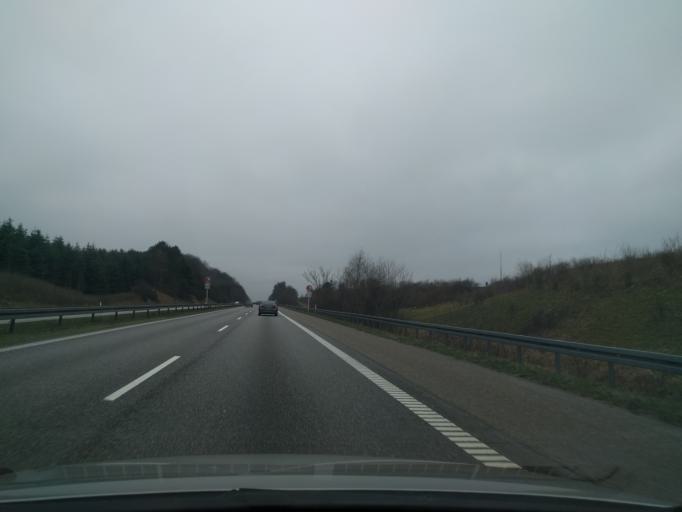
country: DK
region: Zealand
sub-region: Slagelse Kommune
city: Slagelse
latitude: 55.4059
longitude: 11.3986
